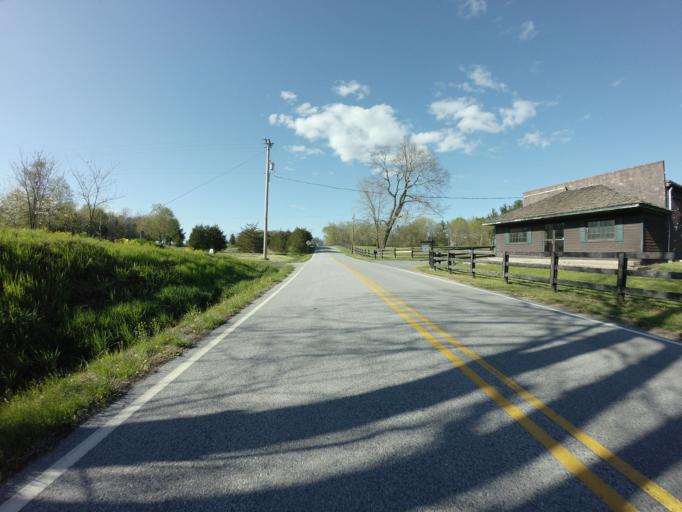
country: US
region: Maryland
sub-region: Frederick County
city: Emmitsburg
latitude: 39.6316
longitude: -77.2861
